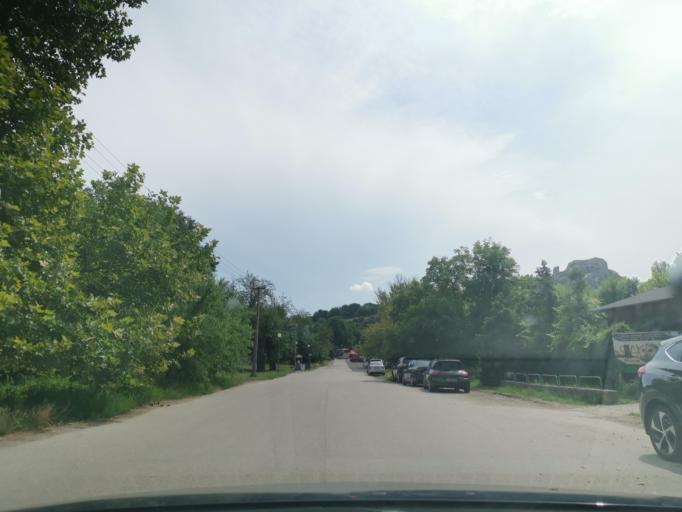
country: AT
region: Lower Austria
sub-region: Politischer Bezirk Bruck an der Leitha
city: Hainburg an der Donau
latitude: 48.1776
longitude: 16.9803
